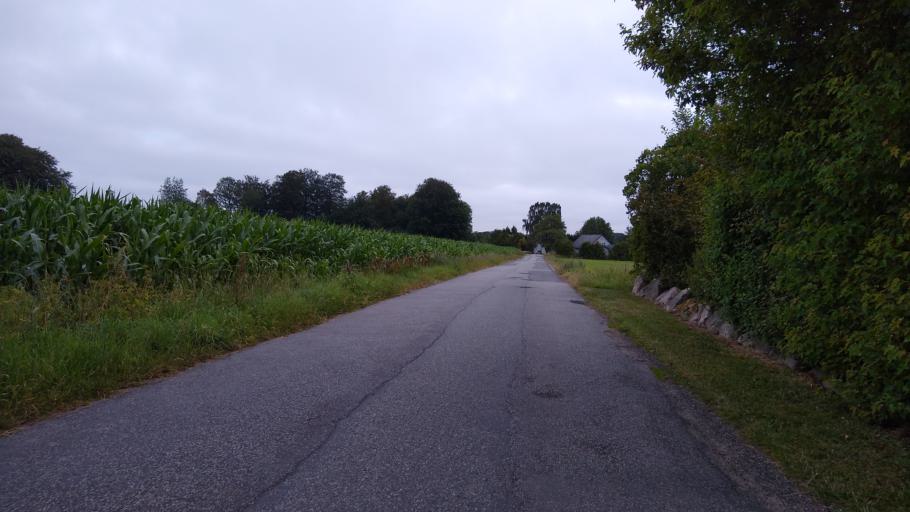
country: DK
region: South Denmark
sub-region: Vejle Kommune
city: Brejning
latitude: 55.6575
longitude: 9.6629
